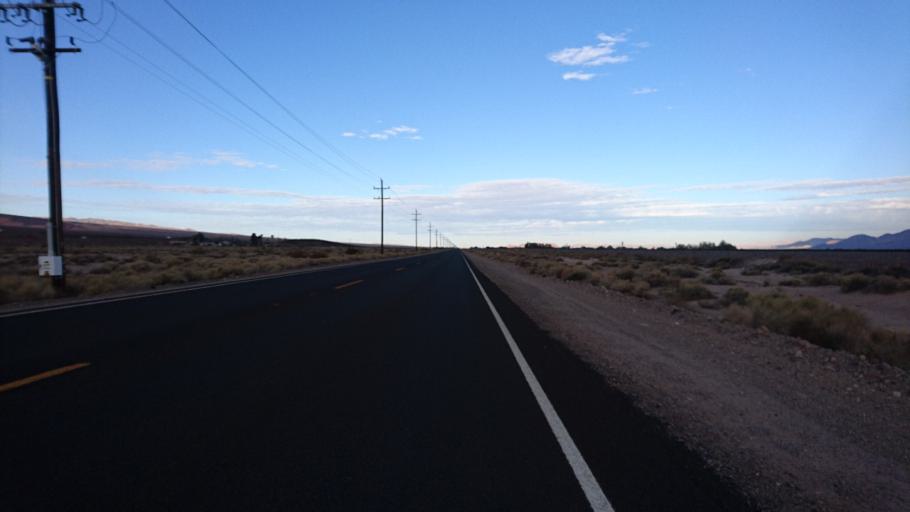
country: US
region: California
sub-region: San Bernardino County
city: Barstow
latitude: 34.8366
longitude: -116.7169
